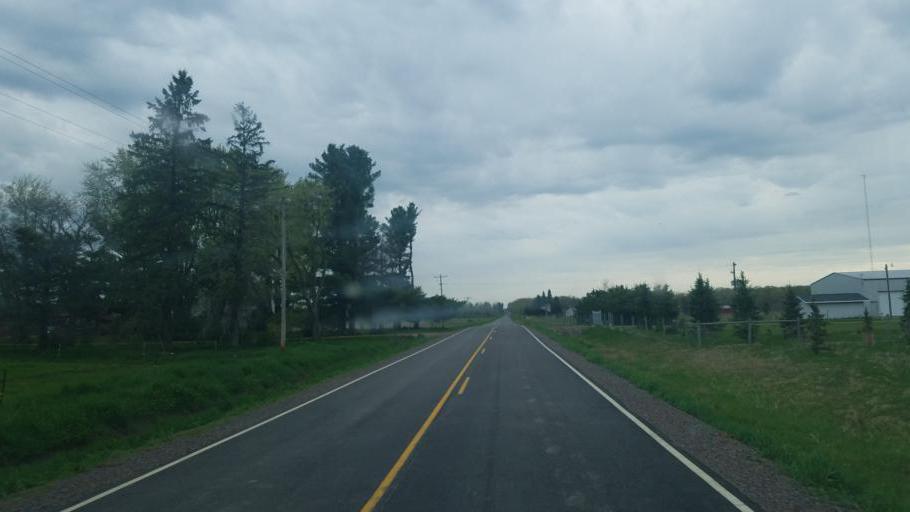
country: US
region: Wisconsin
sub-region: Wood County
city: Marshfield
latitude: 44.4830
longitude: -90.2798
